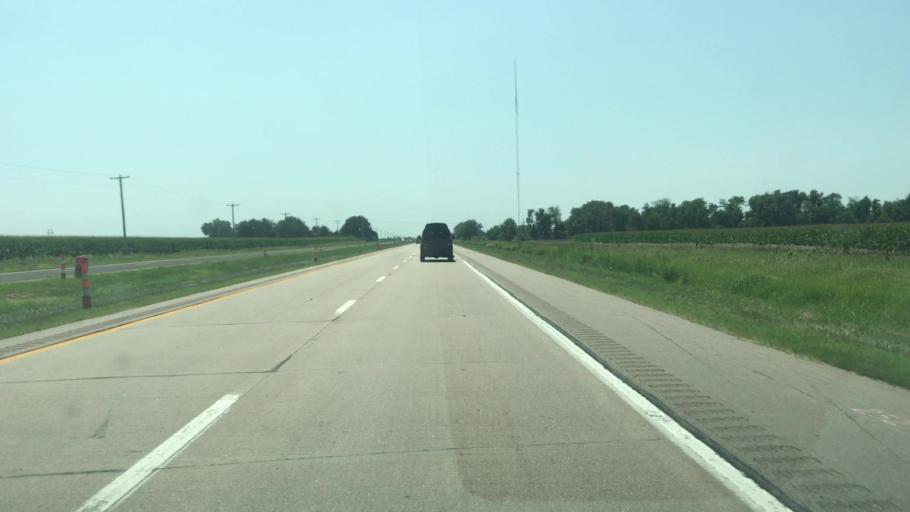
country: US
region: Nebraska
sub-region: Adams County
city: Hastings
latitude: 40.6596
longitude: -98.3824
